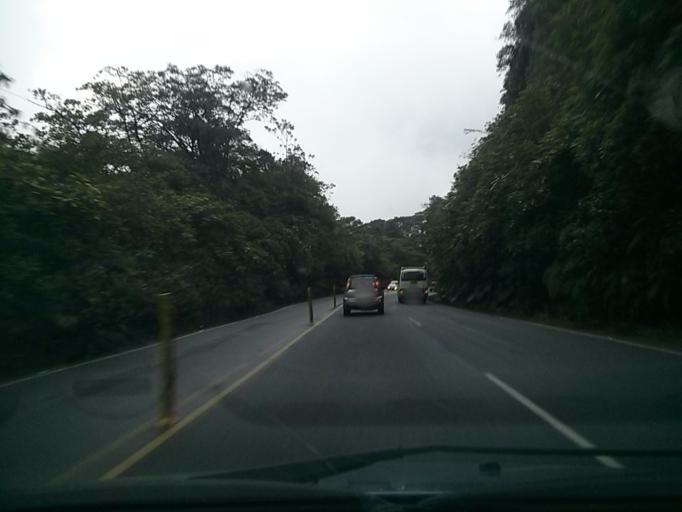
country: CR
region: Heredia
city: Angeles
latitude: 10.0553
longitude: -84.0091
